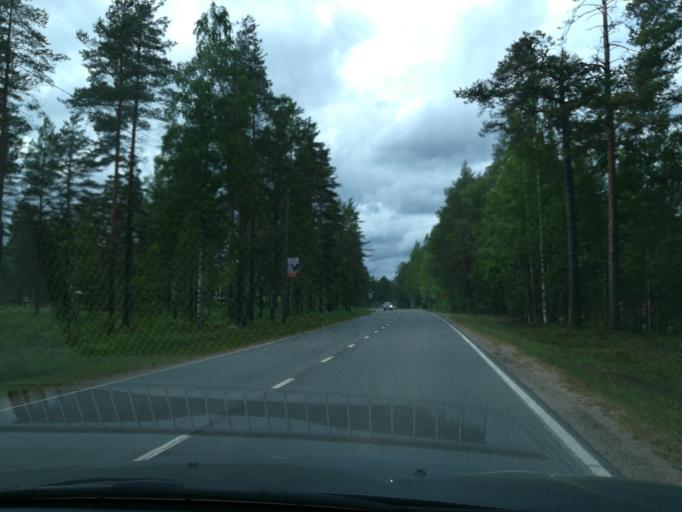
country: FI
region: South Karelia
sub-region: Lappeenranta
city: Savitaipale
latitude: 61.1940
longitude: 27.7059
